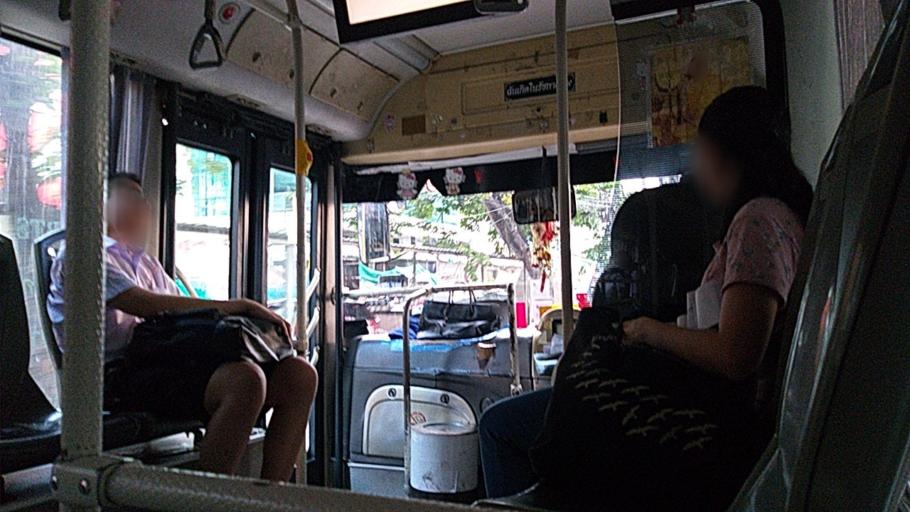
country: TH
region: Bangkok
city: Don Mueang
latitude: 13.9381
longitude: 100.6110
